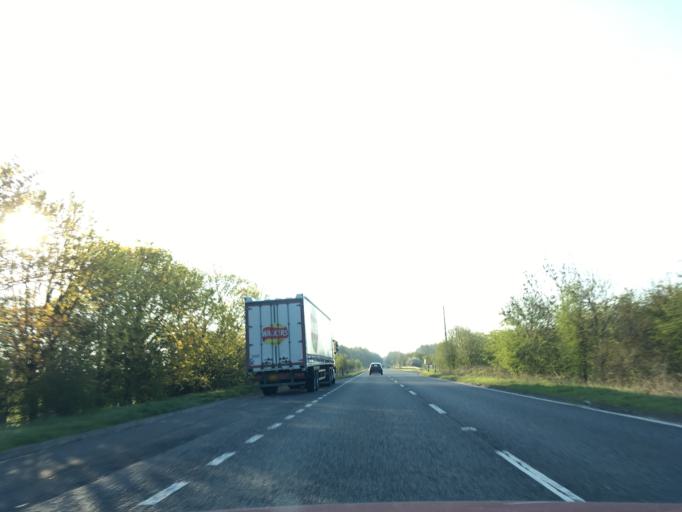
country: GB
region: England
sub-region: Gloucestershire
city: Northleach
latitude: 51.8322
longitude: -1.8203
